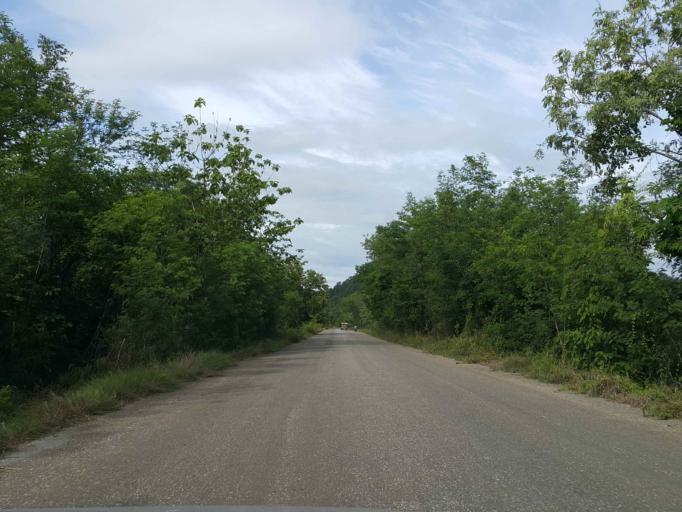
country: TH
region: Sukhothai
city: Thung Saliam
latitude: 17.2599
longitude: 99.5280
